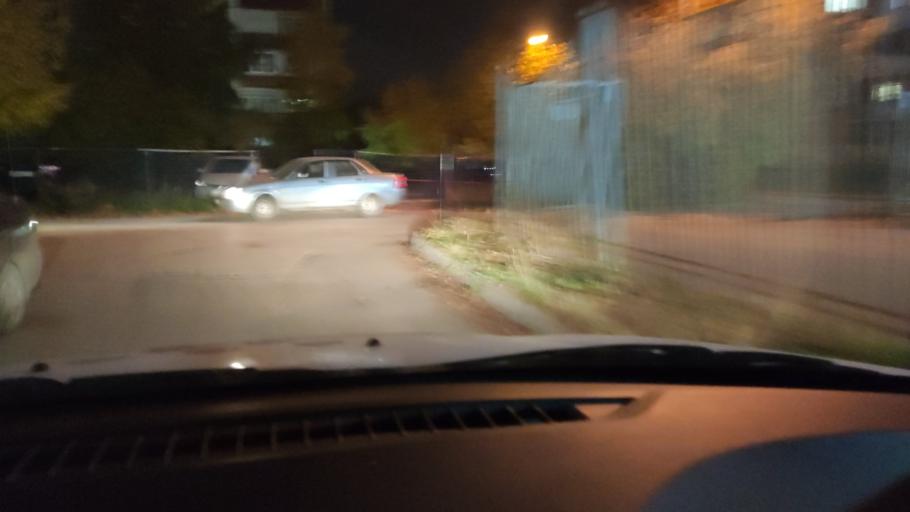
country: RU
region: Perm
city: Kondratovo
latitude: 57.9993
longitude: 56.1546
